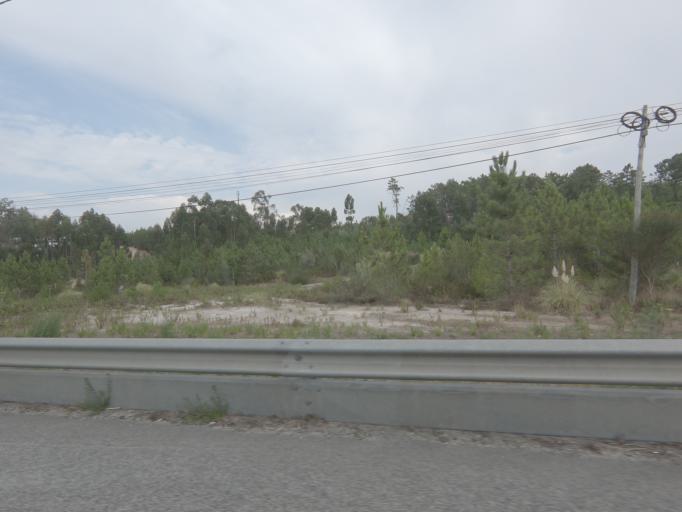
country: PT
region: Coimbra
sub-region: Condeixa-A-Nova
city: Condeixa-a-Nova
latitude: 40.1446
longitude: -8.4649
